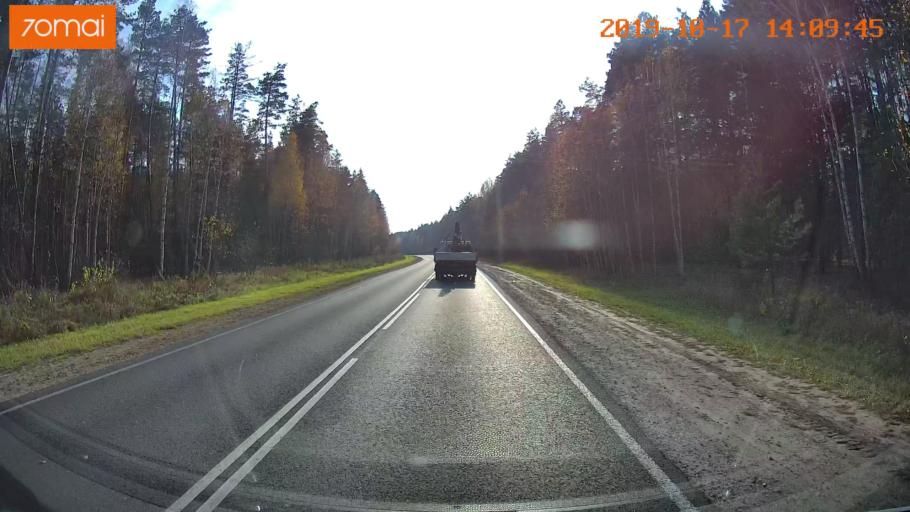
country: RU
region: Rjazan
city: Spas-Klepiki
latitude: 55.0859
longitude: 40.0551
